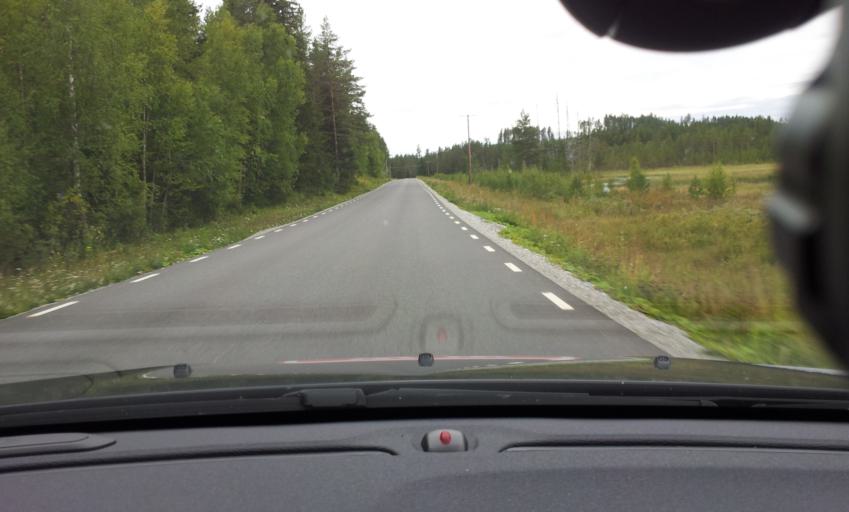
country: SE
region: Jaemtland
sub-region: Braecke Kommun
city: Braecke
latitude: 63.0696
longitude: 15.3600
